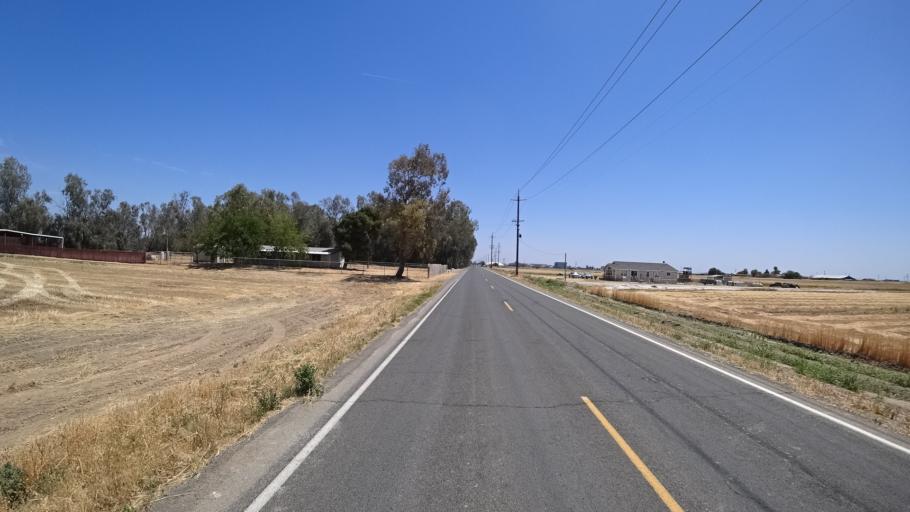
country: US
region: California
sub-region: Kings County
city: Lemoore
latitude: 36.2402
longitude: -119.7858
